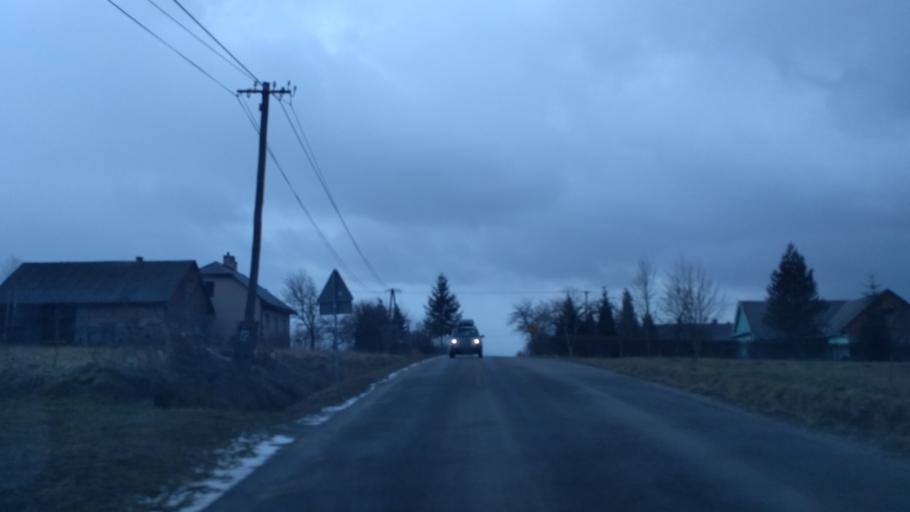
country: PL
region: Subcarpathian Voivodeship
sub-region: Powiat rzeszowski
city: Blazowa
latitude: 49.8509
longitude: 22.0886
